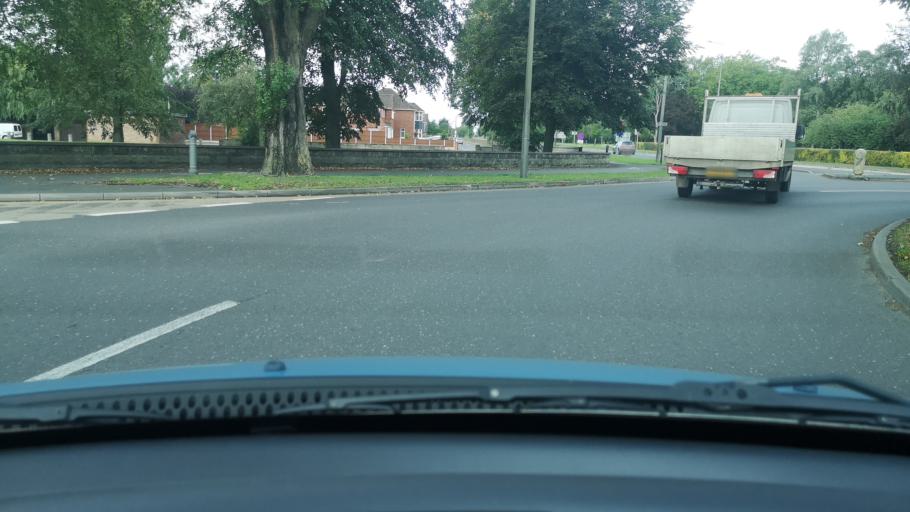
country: GB
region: England
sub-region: North Lincolnshire
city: Scunthorpe
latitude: 53.5788
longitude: -0.6546
